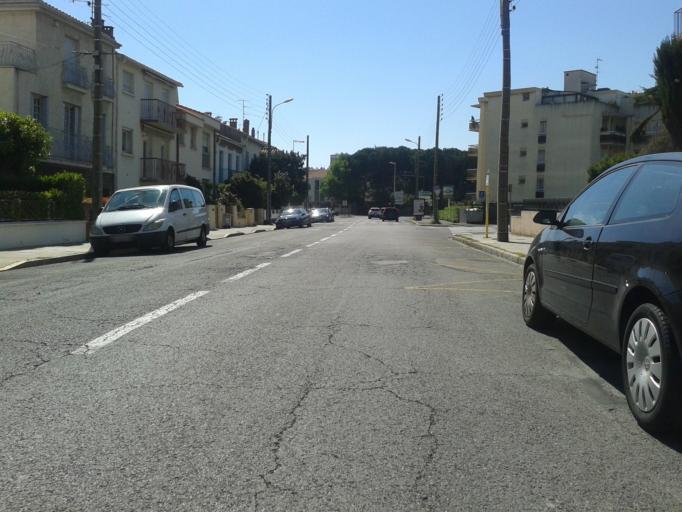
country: FR
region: Languedoc-Roussillon
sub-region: Departement des Pyrenees-Orientales
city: Perpignan
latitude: 42.6885
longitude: 2.9001
